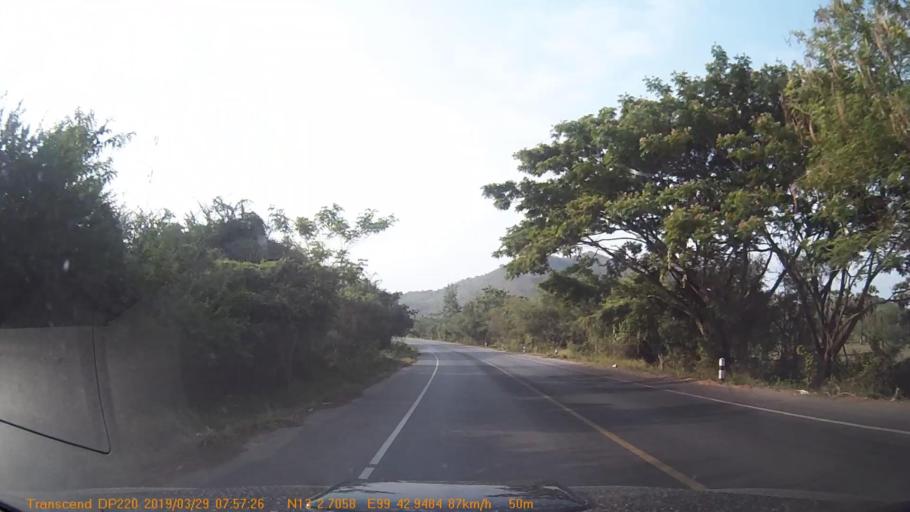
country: TH
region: Phetchaburi
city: Nong Ya Plong
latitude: 13.0447
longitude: 99.7159
